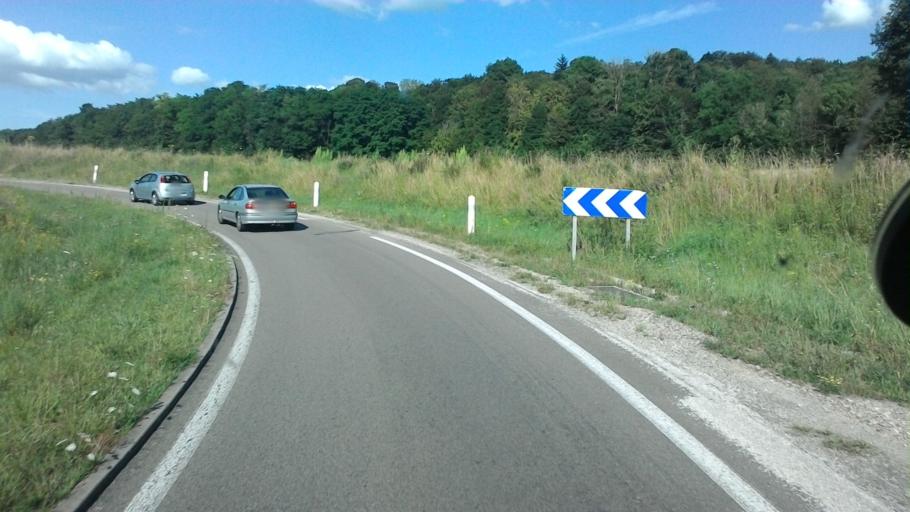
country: FR
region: Franche-Comte
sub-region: Departement de la Haute-Saone
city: Noidans-les-Vesoul
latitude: 47.5976
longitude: 6.1117
